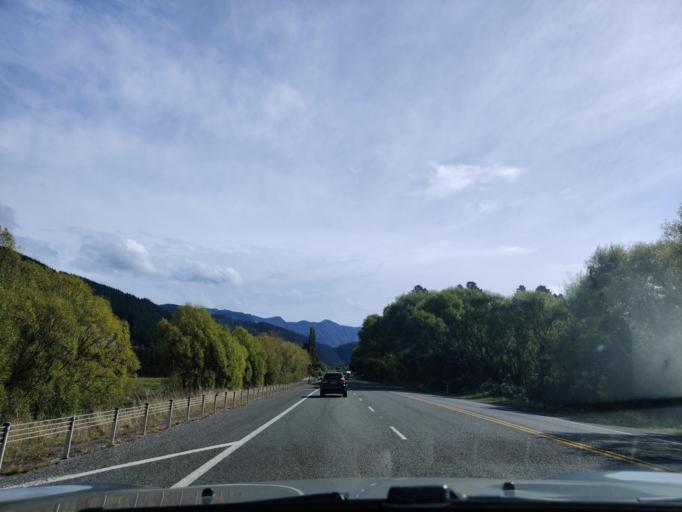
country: NZ
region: Marlborough
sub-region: Marlborough District
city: Picton
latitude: -41.3826
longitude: 173.9495
